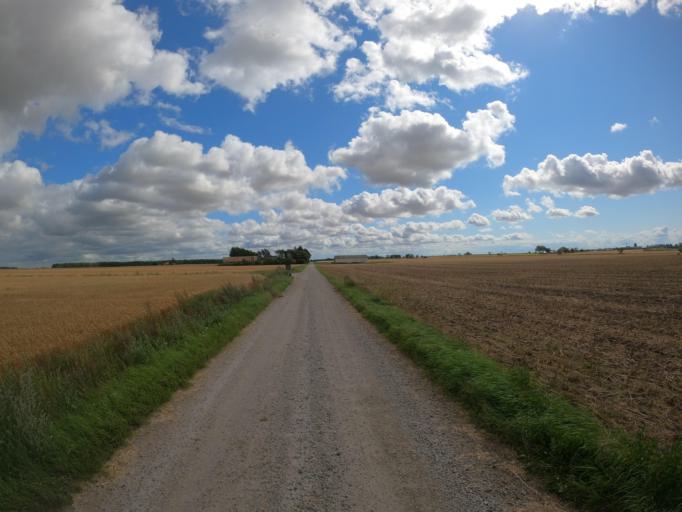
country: SE
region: Skane
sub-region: Lunds Kommun
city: Lund
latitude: 55.7327
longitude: 13.2610
